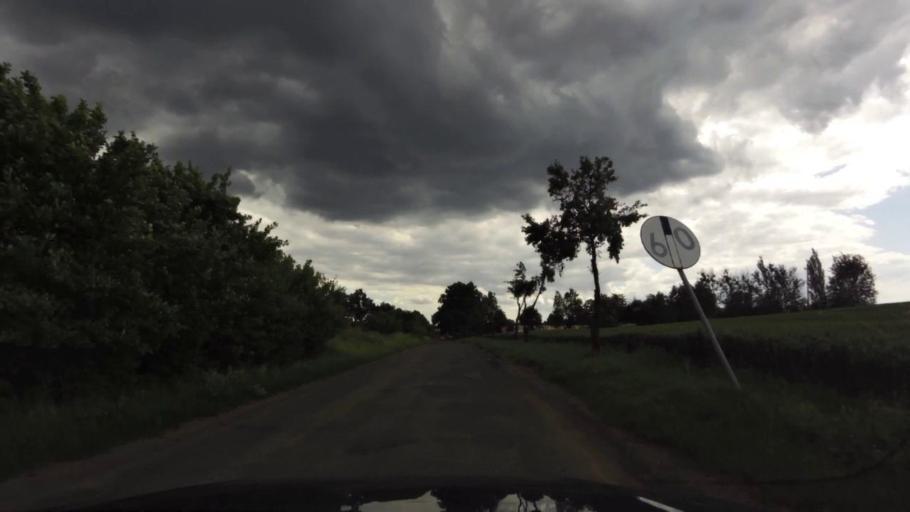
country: PL
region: West Pomeranian Voivodeship
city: Trzcinsko Zdroj
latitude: 52.9170
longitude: 14.5962
